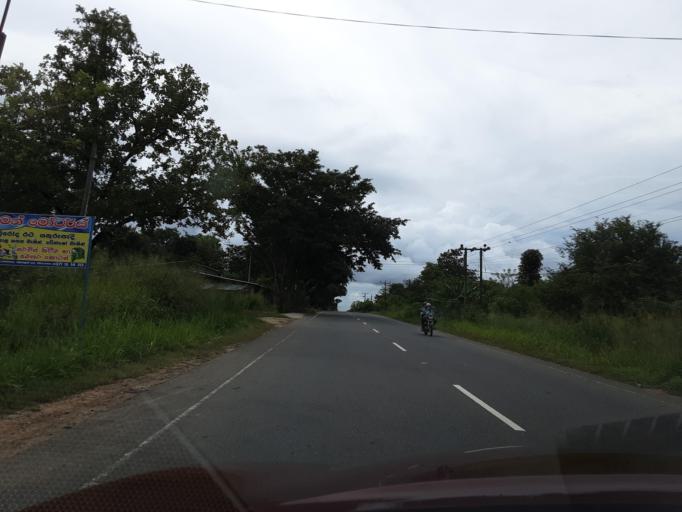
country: LK
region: Uva
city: Badulla
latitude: 7.3895
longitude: 81.1394
